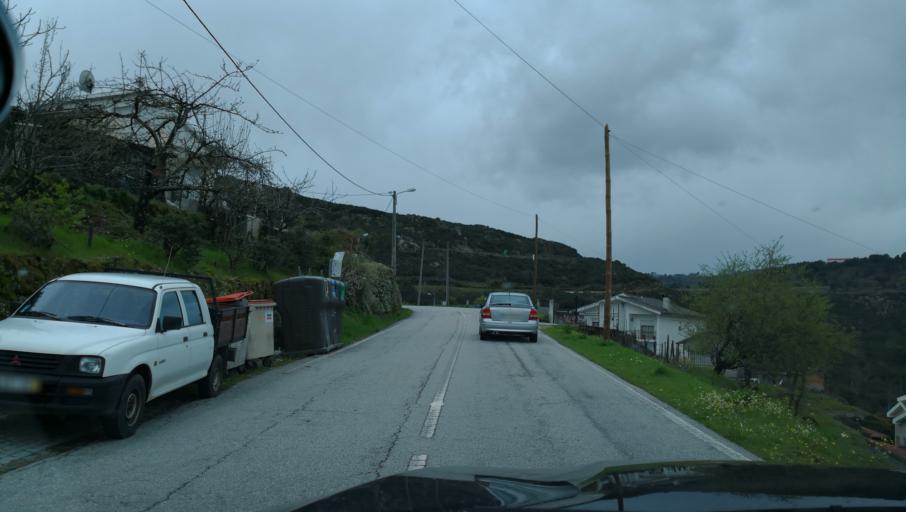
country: PT
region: Vila Real
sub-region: Vila Real
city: Vila Real
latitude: 41.2783
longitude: -7.7804
